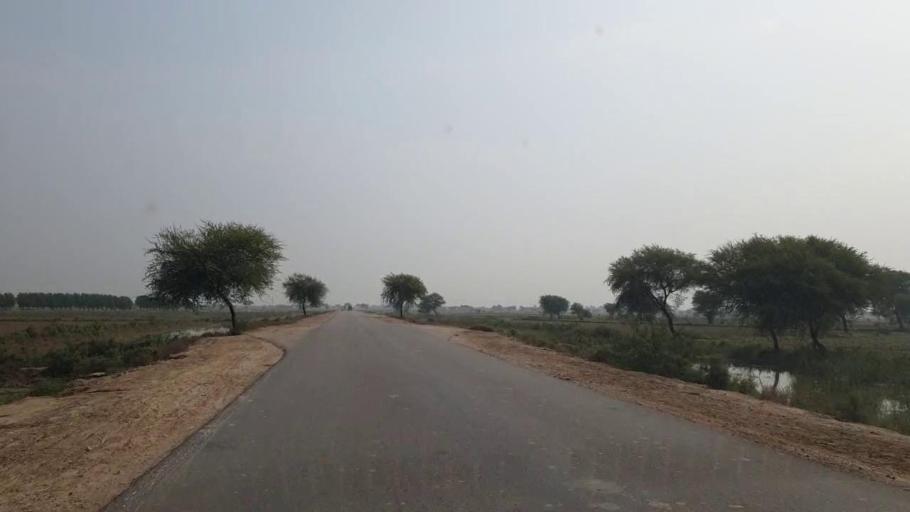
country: PK
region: Sindh
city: Matli
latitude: 25.0605
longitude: 68.6680
